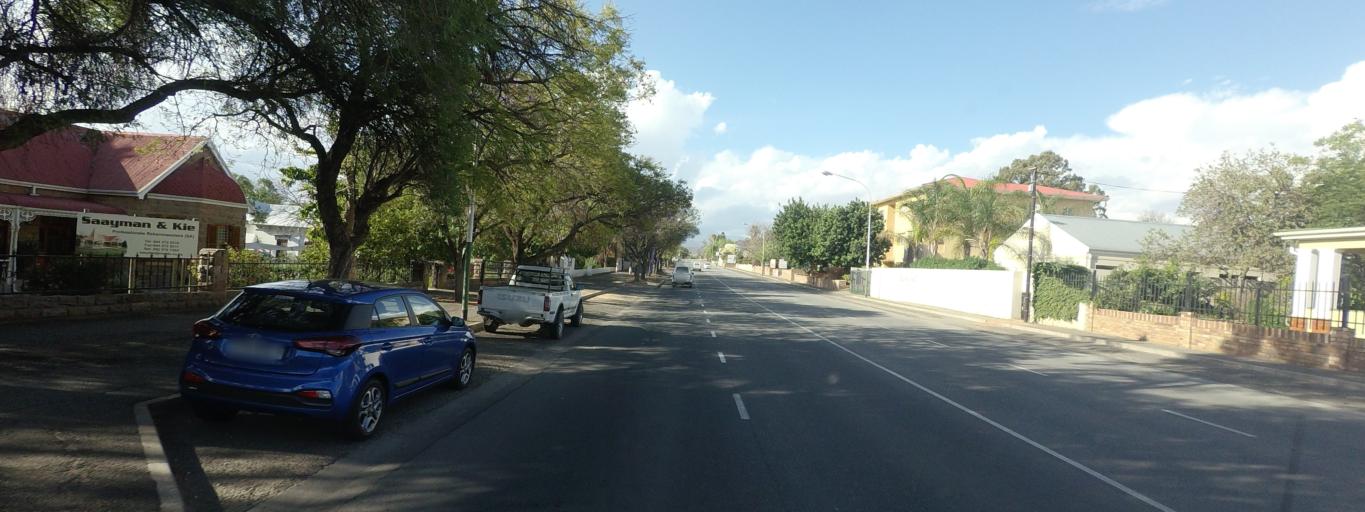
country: ZA
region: Western Cape
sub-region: Eden District Municipality
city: Oudtshoorn
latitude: -33.5820
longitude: 22.2046
